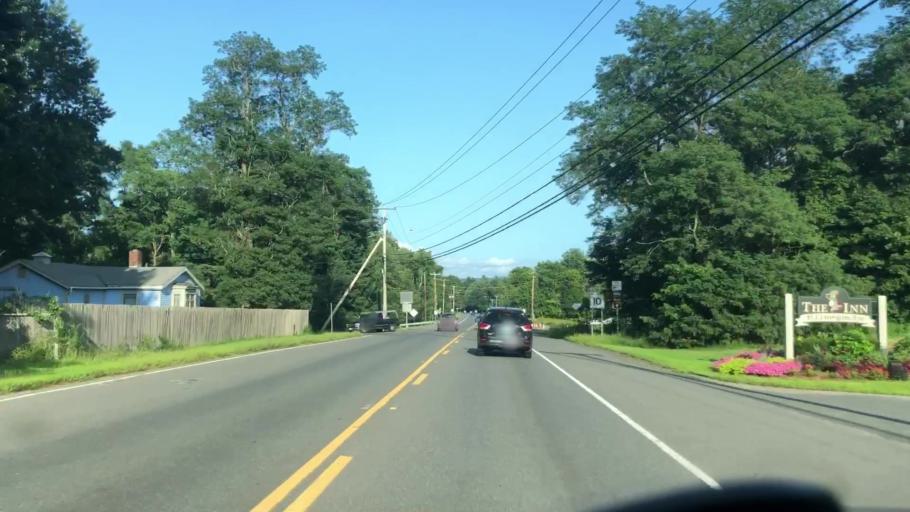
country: US
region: Massachusetts
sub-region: Franklin County
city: Bernardston
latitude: 42.6704
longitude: -72.5399
